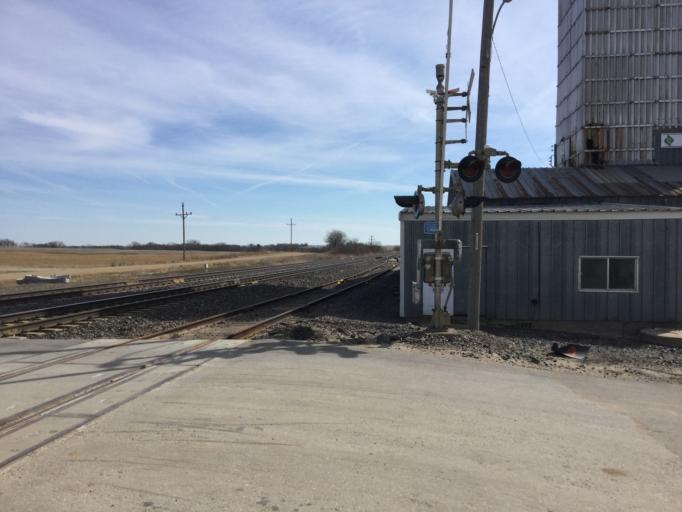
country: US
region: Kansas
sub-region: Marshall County
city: Marysville
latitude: 39.8894
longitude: -96.7125
